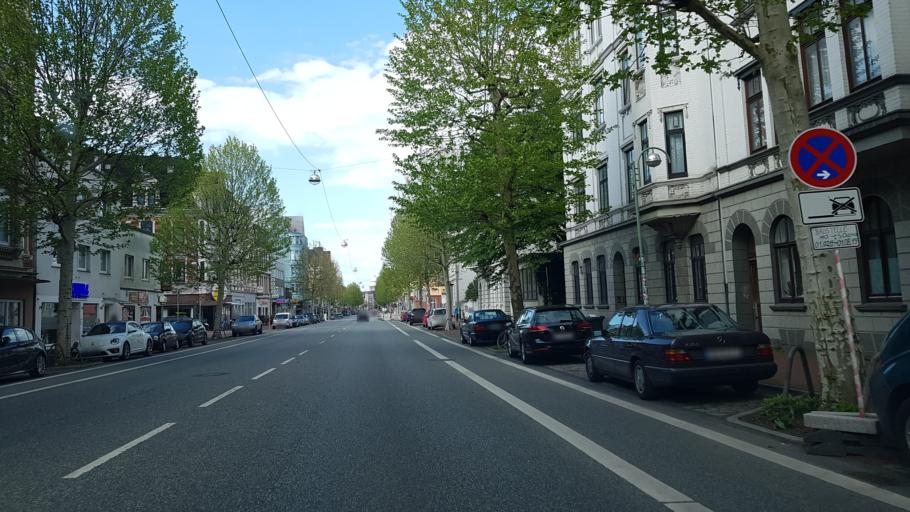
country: DE
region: Bremen
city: Bremerhaven
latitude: 53.5528
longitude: 8.5817
